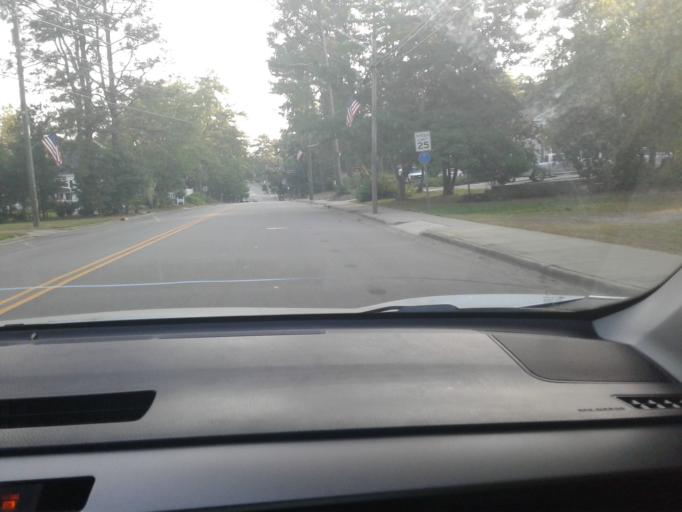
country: US
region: North Carolina
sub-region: Wake County
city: Fuquay-Varina
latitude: 35.5778
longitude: -78.8000
